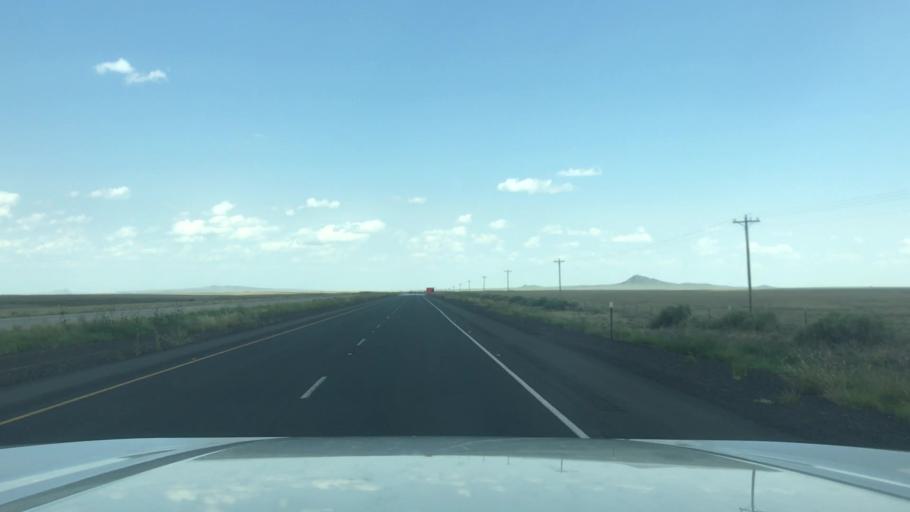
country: US
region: New Mexico
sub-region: Union County
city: Clayton
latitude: 36.6317
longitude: -103.7146
